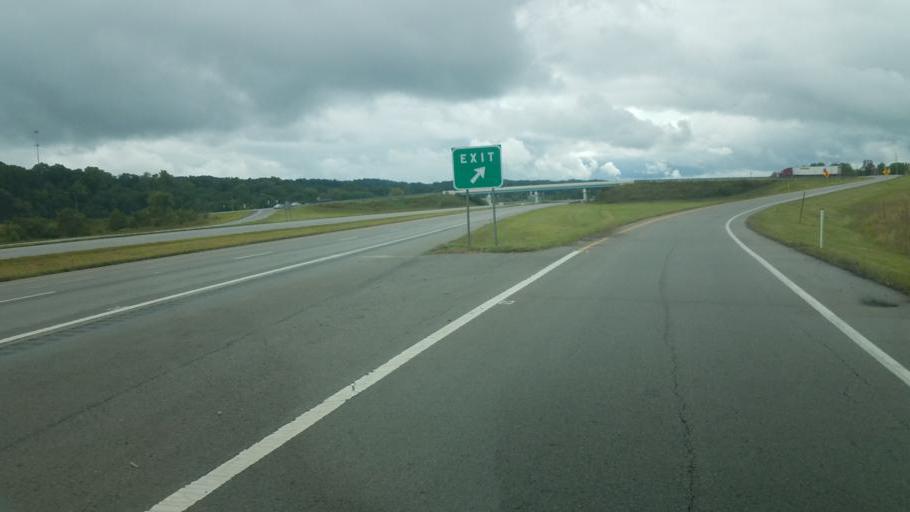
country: US
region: Ohio
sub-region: Scioto County
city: Wheelersburg
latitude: 38.6936
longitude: -82.8619
